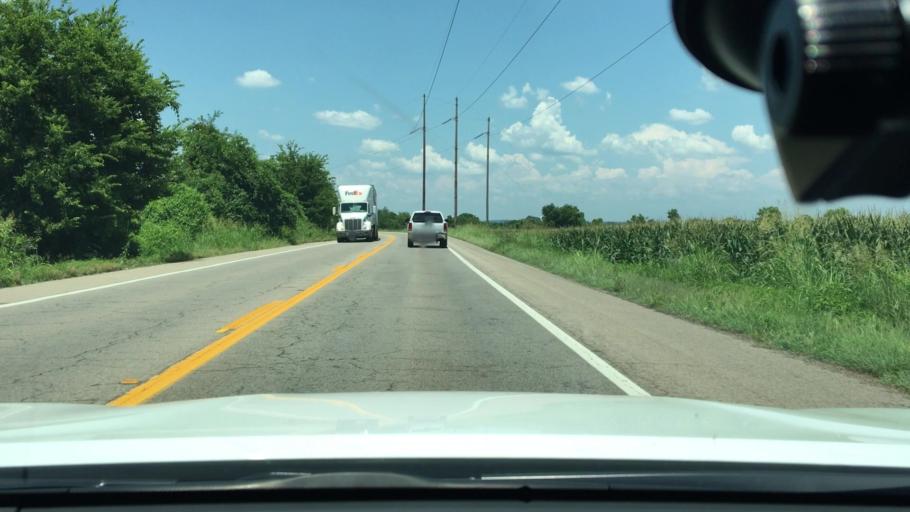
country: US
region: Arkansas
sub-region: Crawford County
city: Van Buren
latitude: 35.3892
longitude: -94.3294
